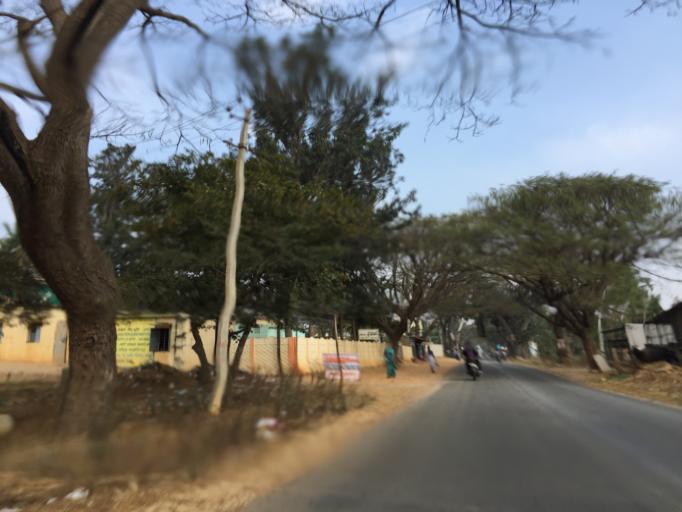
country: IN
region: Karnataka
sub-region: Bangalore Rural
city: Devanhalli
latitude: 13.3287
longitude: 77.6916
